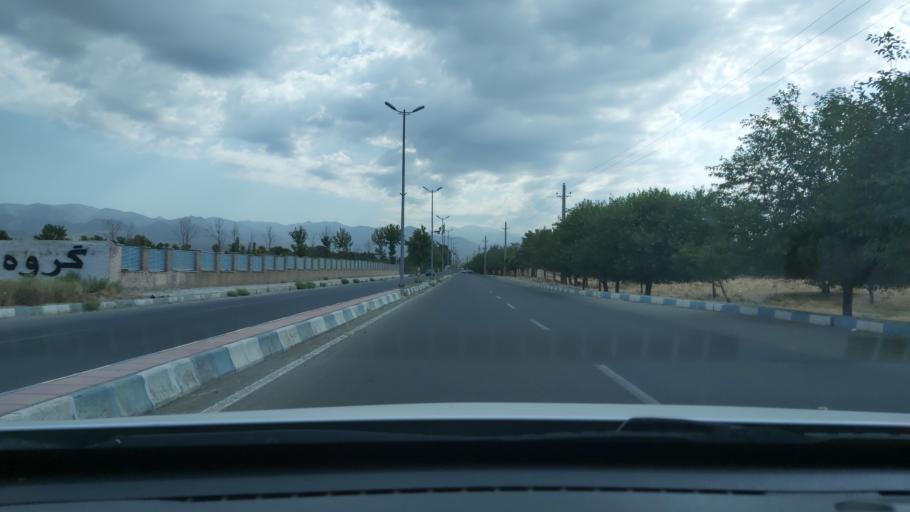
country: IR
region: Alborz
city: Hashtgerd
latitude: 35.9398
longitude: 50.7663
